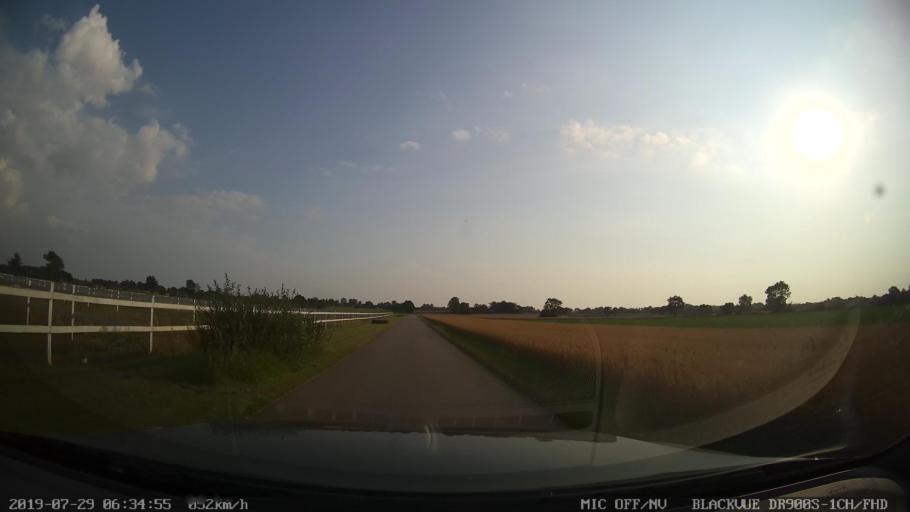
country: SE
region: Skane
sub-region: Helsingborg
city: Odakra
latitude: 56.1168
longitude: 12.7223
